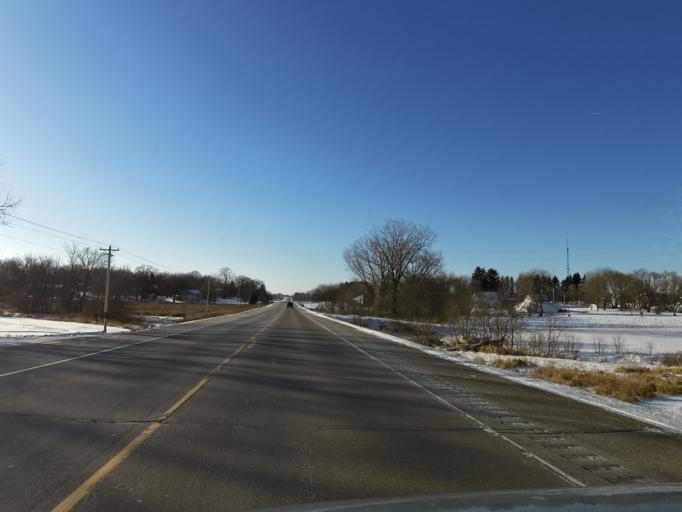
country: US
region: Minnesota
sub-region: Le Sueur County
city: New Prague
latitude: 44.5437
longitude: -93.5261
